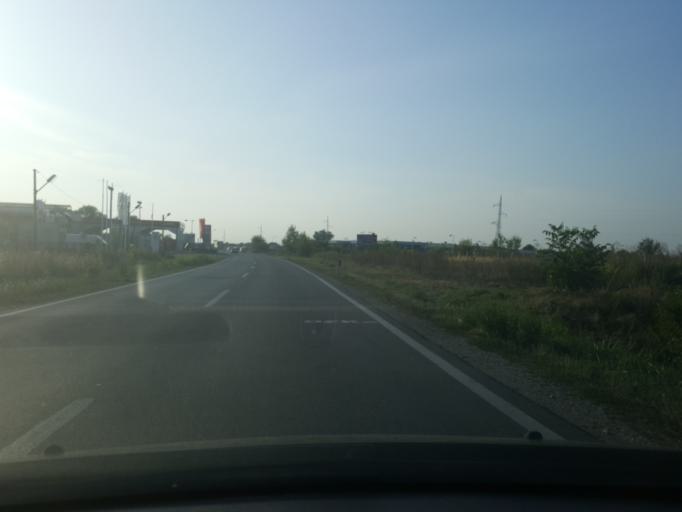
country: RS
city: Majur
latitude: 44.7617
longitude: 19.6420
